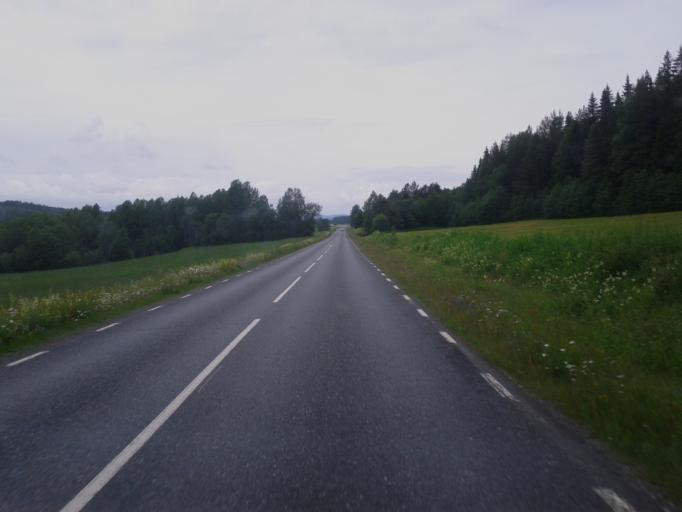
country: SE
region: Vaesterbotten
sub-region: Skelleftea Kommun
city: Viken
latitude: 64.8874
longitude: 20.7528
